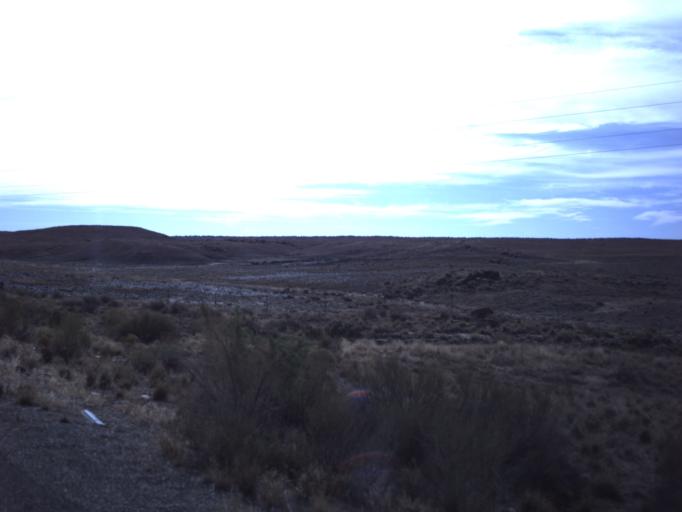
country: US
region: Utah
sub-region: San Juan County
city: Blanding
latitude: 37.4179
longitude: -109.4321
